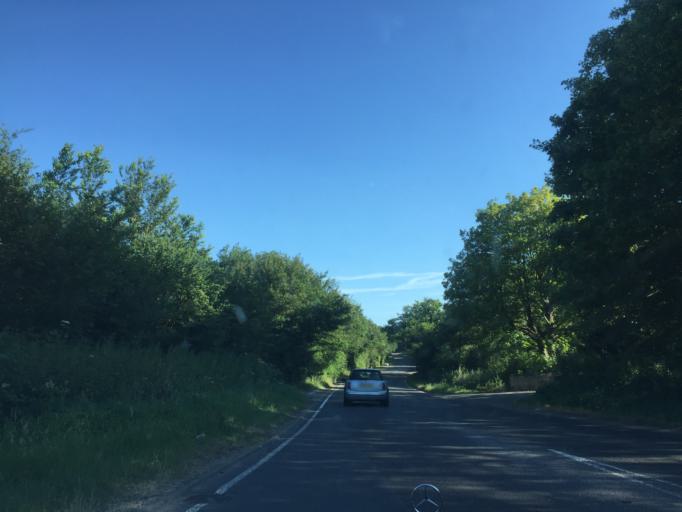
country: GB
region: England
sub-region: Oxfordshire
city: Wheatley
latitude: 51.7383
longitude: -1.0816
